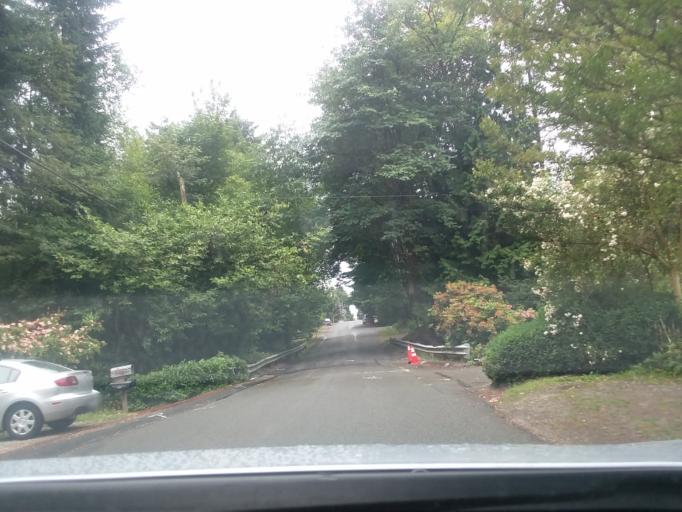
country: US
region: Washington
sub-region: King County
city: Lake Forest Park
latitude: 47.7182
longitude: -122.3019
